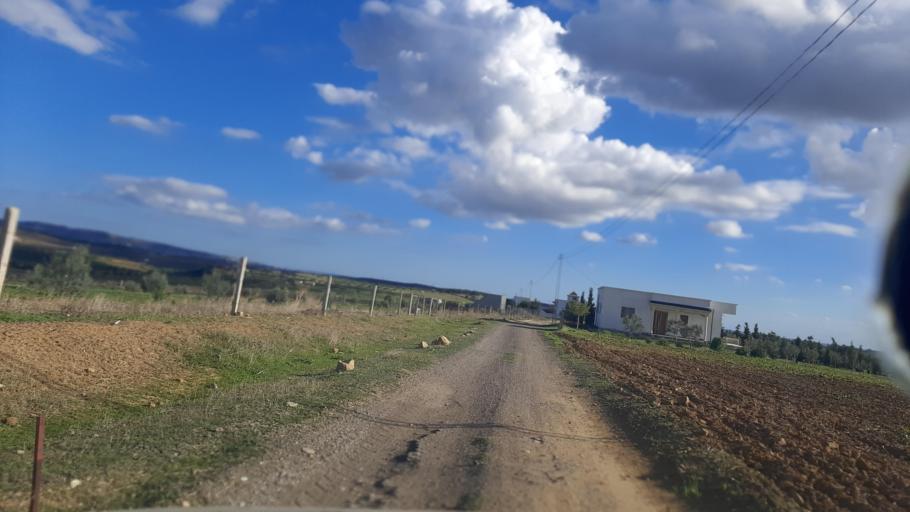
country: TN
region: Nabul
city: Bu `Urqub
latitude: 36.4675
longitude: 10.4797
